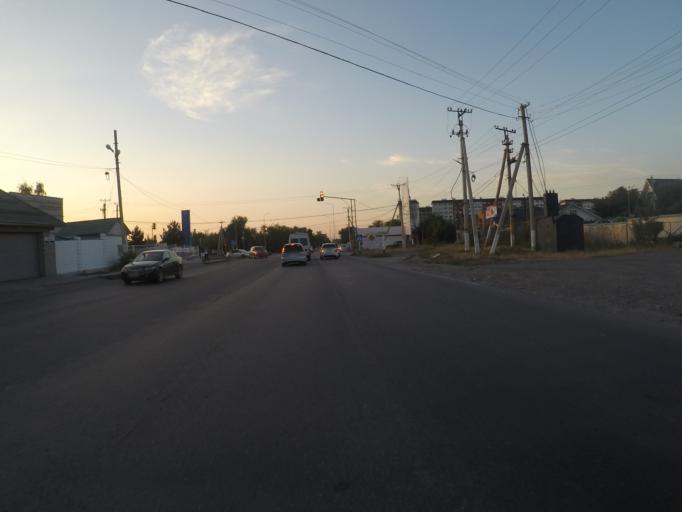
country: KG
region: Chuy
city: Lebedinovka
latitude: 42.8119
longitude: 74.6457
